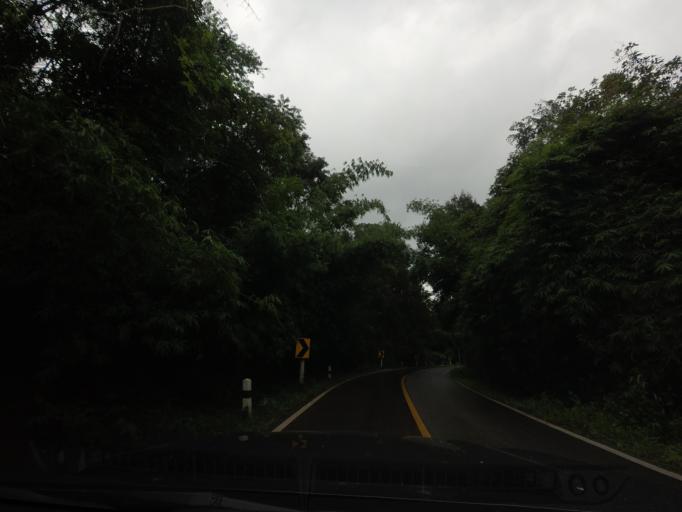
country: TH
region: Nong Khai
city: Sangkhom
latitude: 18.0271
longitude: 102.3459
